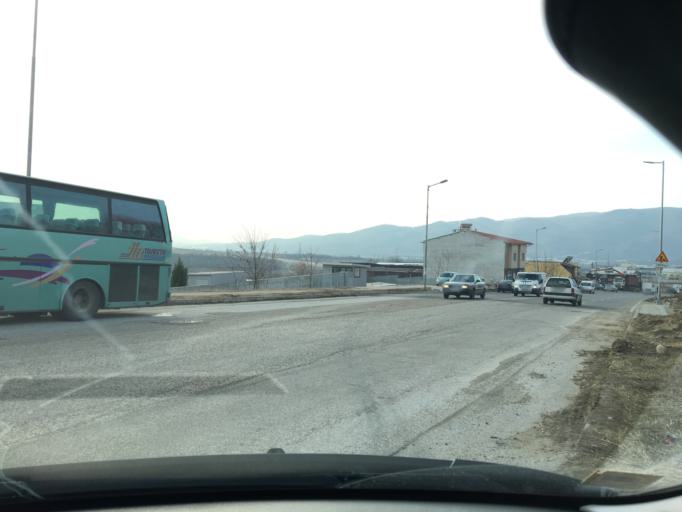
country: BG
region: Blagoevgrad
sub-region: Obshtina Sandanski
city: Sandanski
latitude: 41.5434
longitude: 23.2601
